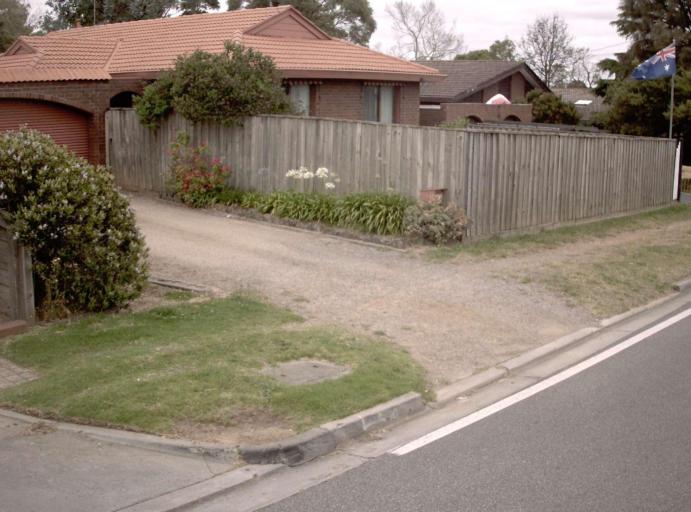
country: AU
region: Victoria
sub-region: Mornington Peninsula
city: Mount Eliza
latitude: -38.2004
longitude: 145.0824
